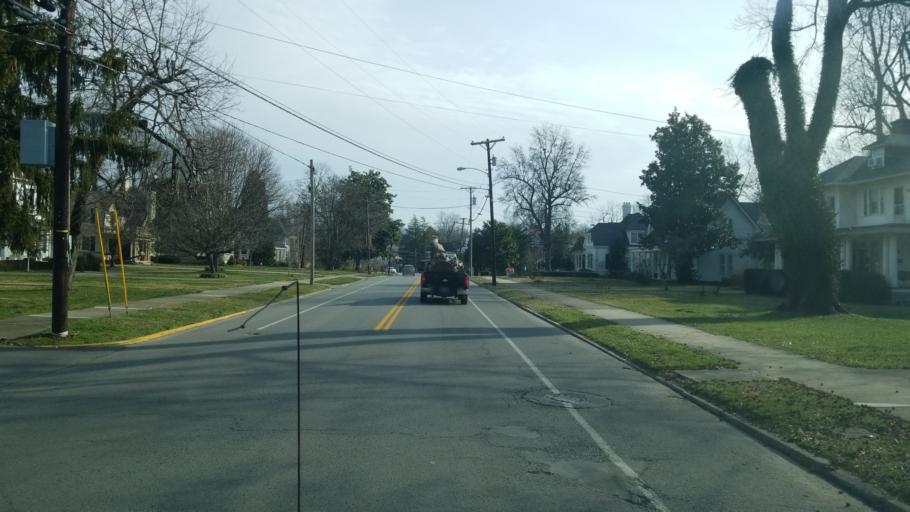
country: US
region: Kentucky
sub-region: Boyle County
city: Danville
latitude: 37.6486
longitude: -84.7660
